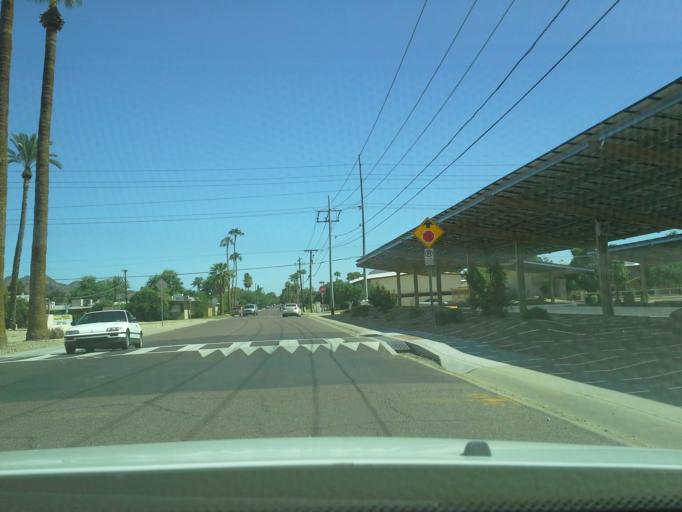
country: US
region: Arizona
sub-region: Maricopa County
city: Phoenix
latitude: 33.5273
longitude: -112.0572
